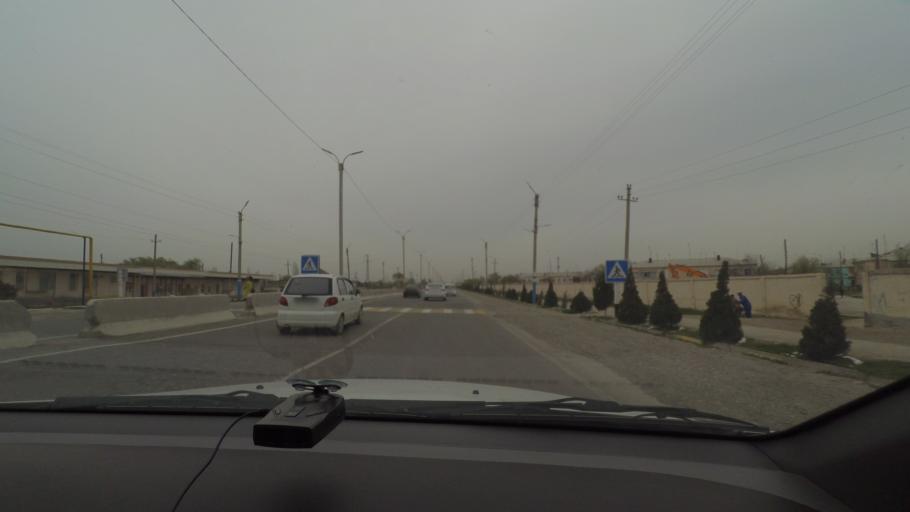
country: KZ
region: Ongtustik Qazaqstan
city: Myrzakent
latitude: 40.5451
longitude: 68.4122
